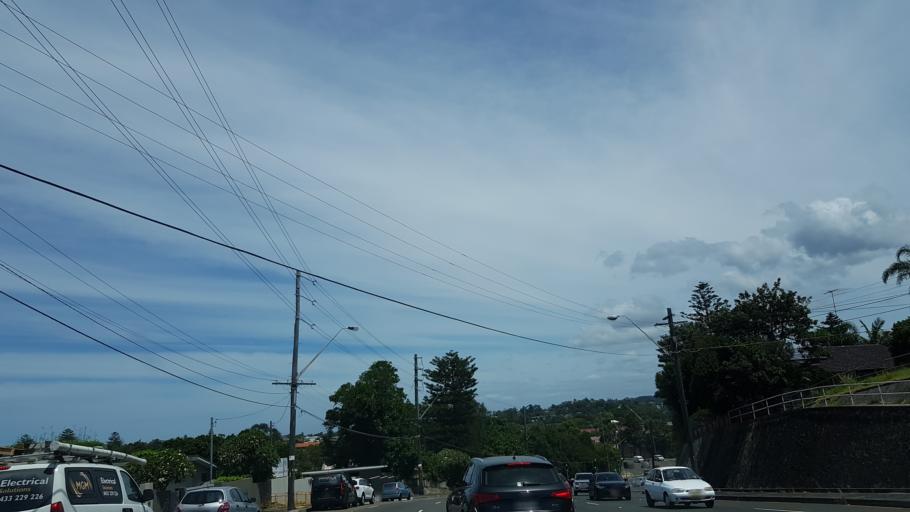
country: AU
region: New South Wales
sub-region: Pittwater
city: Bay View
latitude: -33.6728
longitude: 151.3127
